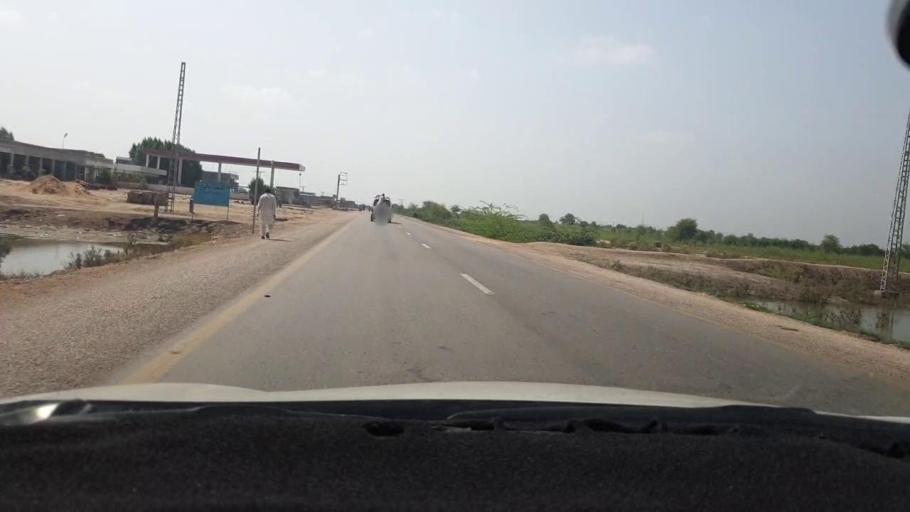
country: PK
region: Sindh
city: Mirpur Khas
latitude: 25.6104
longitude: 69.0830
